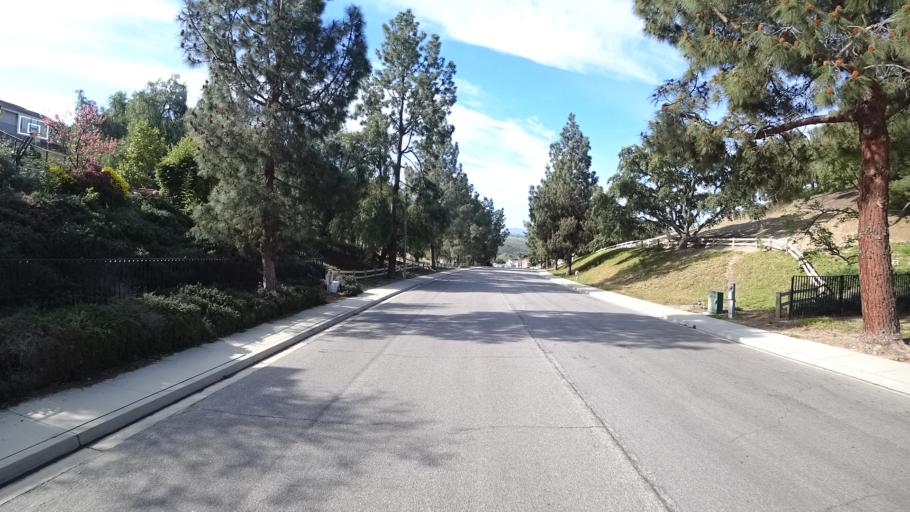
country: US
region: California
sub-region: Ventura County
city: Thousand Oaks
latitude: 34.2152
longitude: -118.8309
